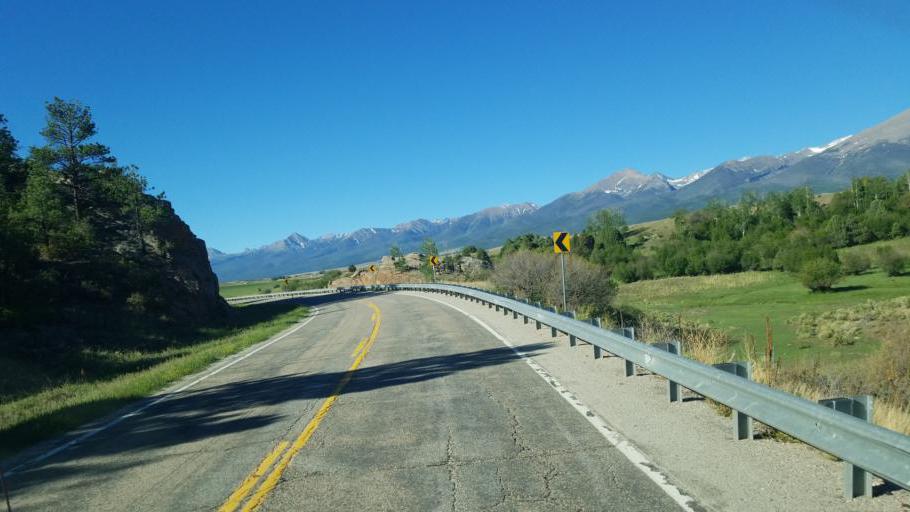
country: US
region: Colorado
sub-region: Custer County
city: Westcliffe
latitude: 38.2290
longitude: -105.5549
